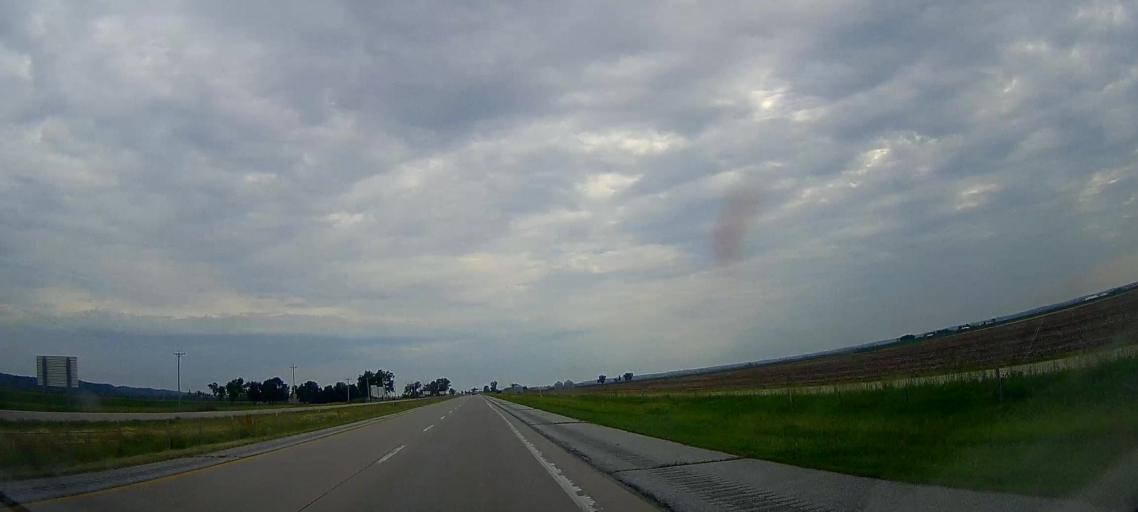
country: US
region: Iowa
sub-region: Harrison County
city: Missouri Valley
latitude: 41.5347
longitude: -95.9179
